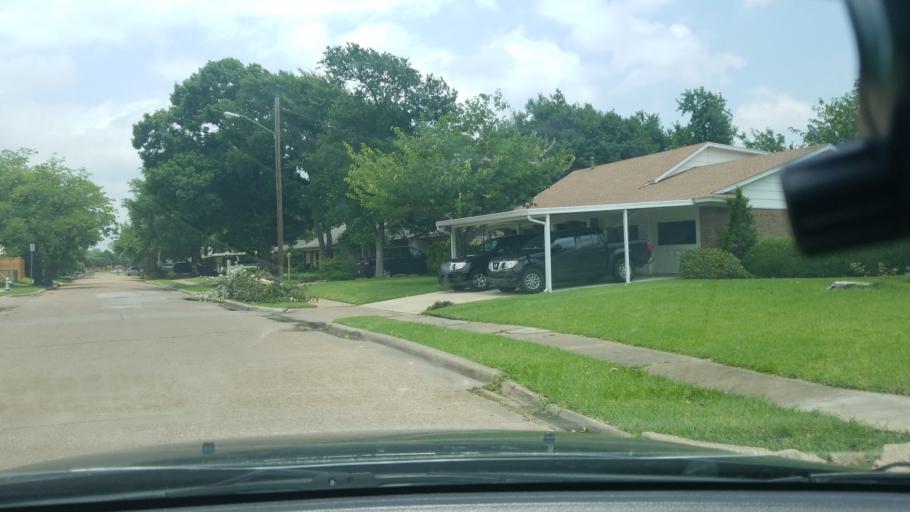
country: US
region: Texas
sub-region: Dallas County
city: Mesquite
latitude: 32.7940
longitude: -96.6467
